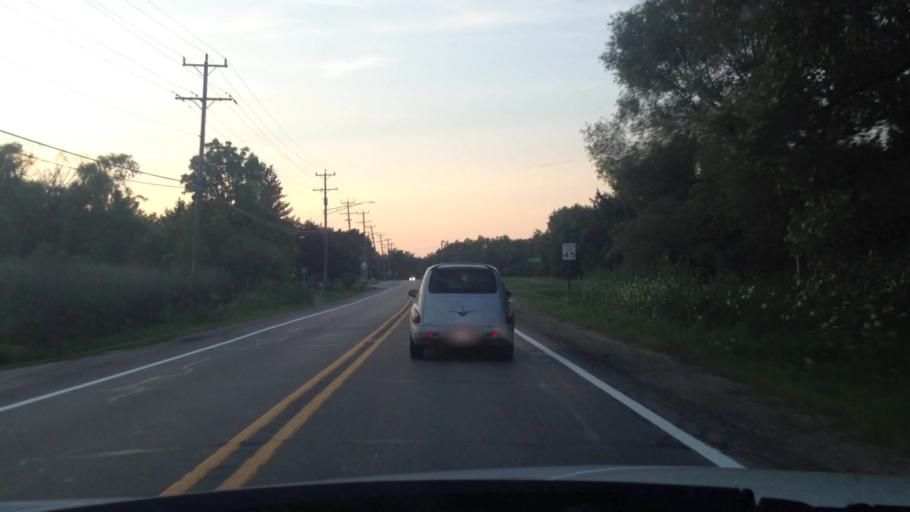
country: US
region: Michigan
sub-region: Oakland County
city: Lake Orion
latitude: 42.7457
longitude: -83.3072
